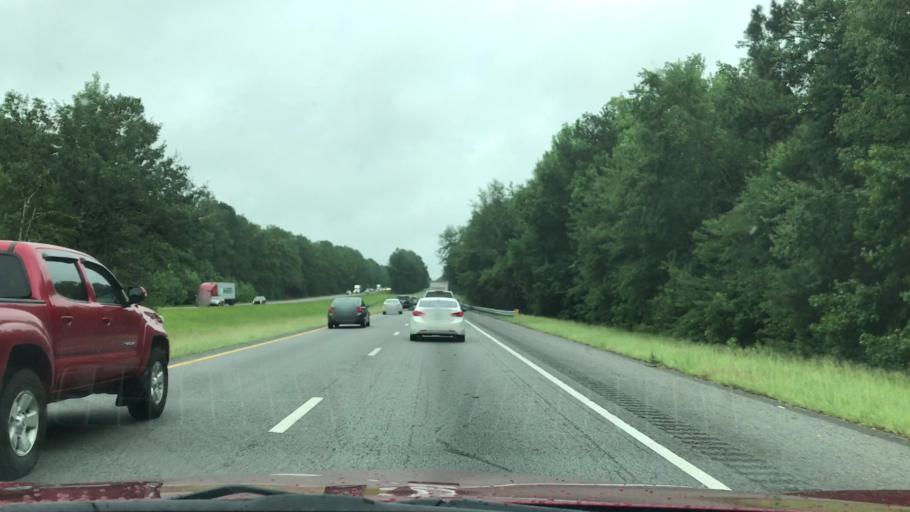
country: US
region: South Carolina
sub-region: Dorchester County
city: Ridgeville
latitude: 33.1674
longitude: -80.3618
